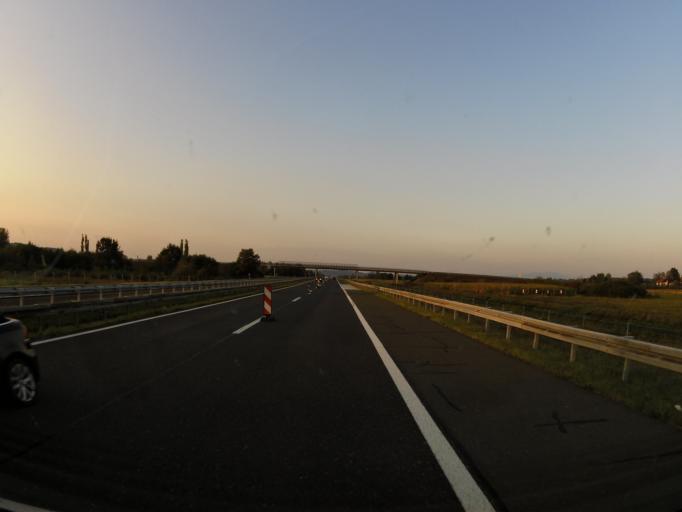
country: HR
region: Zagrebacka
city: Jakovlje
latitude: 45.9725
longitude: 15.8530
